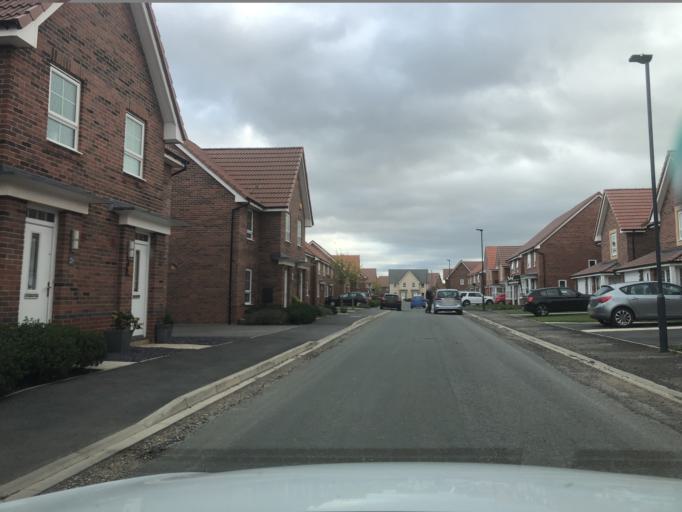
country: GB
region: England
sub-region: North Yorkshire
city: Northallerton
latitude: 54.3444
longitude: -1.4450
